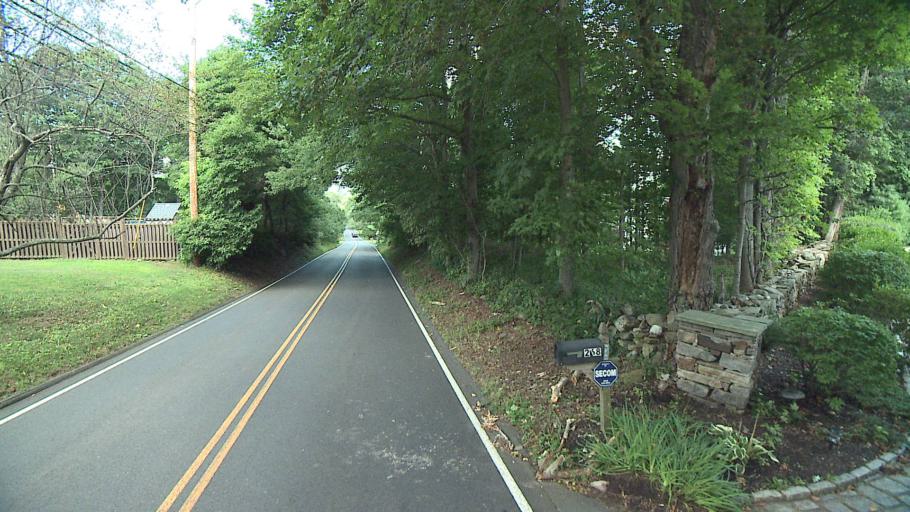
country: US
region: Connecticut
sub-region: Fairfield County
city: Trumbull
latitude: 41.2798
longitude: -73.1583
